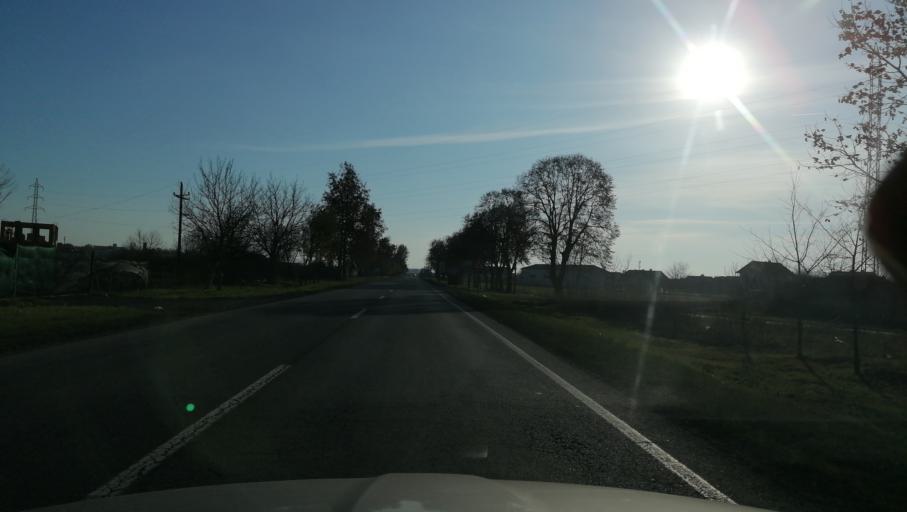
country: RS
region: Autonomna Pokrajina Vojvodina
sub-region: Sremski Okrug
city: Sremska Mitrovica
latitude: 44.9794
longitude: 19.6386
